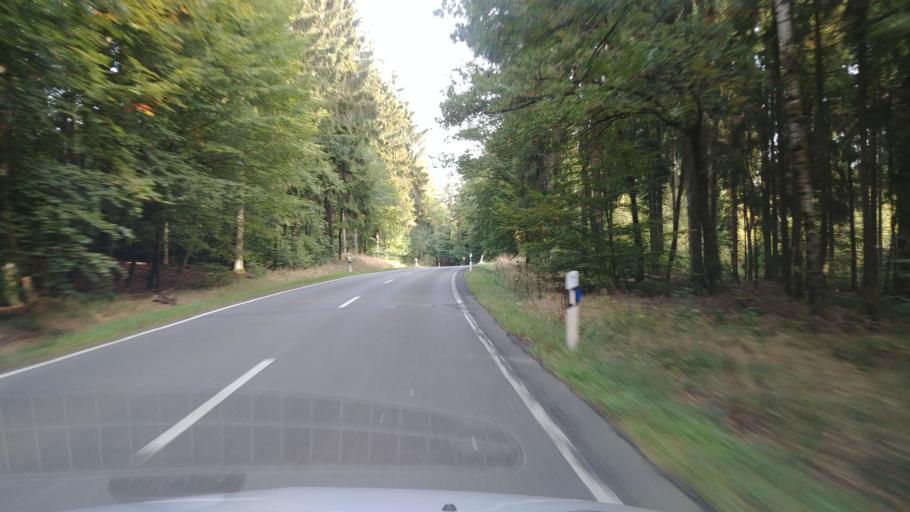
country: DE
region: Rheinland-Pfalz
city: Reckenroth
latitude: 50.1785
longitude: 8.0106
